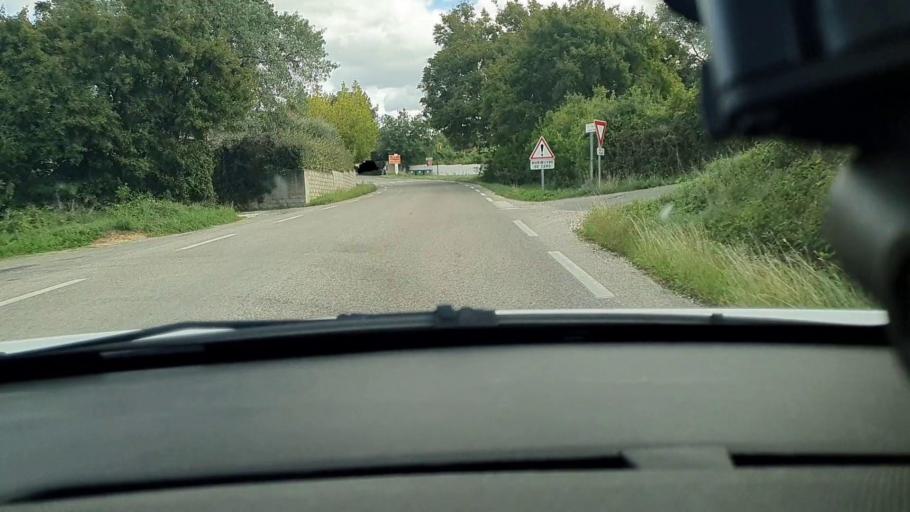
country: FR
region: Languedoc-Roussillon
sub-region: Departement du Gard
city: Salindres
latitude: 44.1871
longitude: 4.2210
